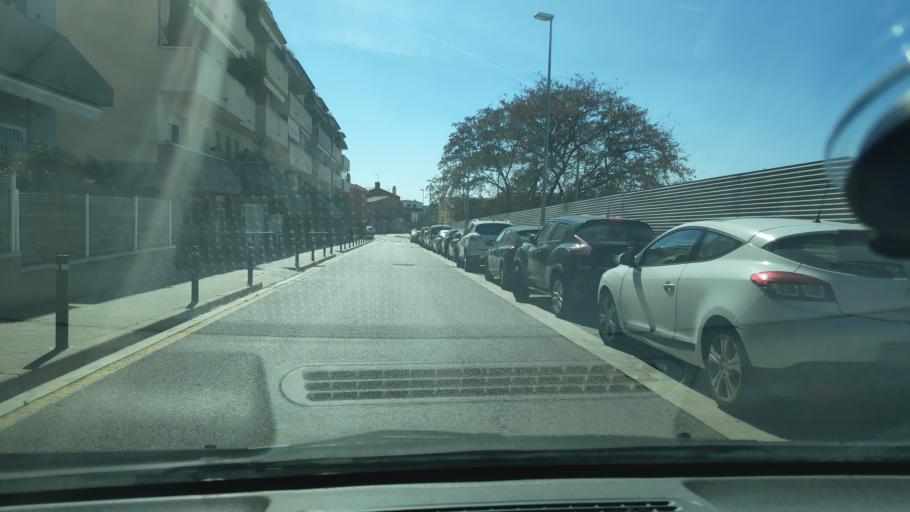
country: ES
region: Catalonia
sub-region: Provincia de Barcelona
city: Rubi
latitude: 41.5037
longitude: 2.0464
